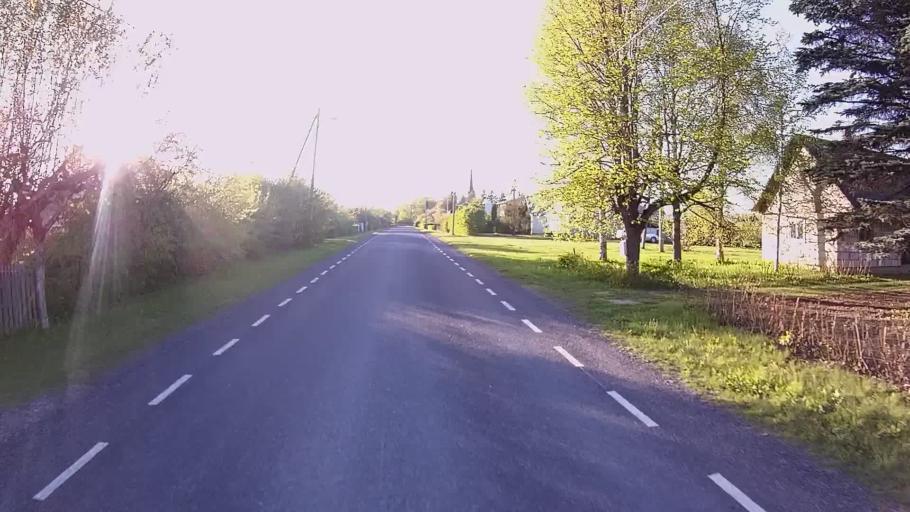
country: EE
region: Jogevamaa
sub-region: Poltsamaa linn
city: Poltsamaa
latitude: 58.5298
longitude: 25.9500
